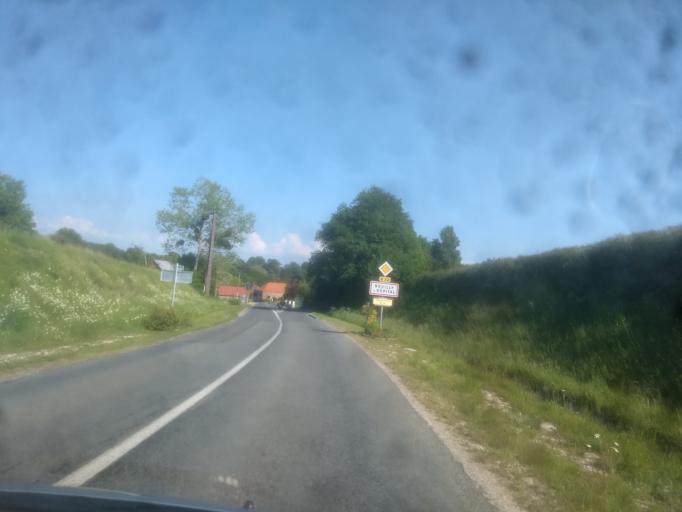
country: FR
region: Picardie
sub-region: Departement de la Somme
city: Abbeville
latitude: 50.1716
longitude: 1.8708
